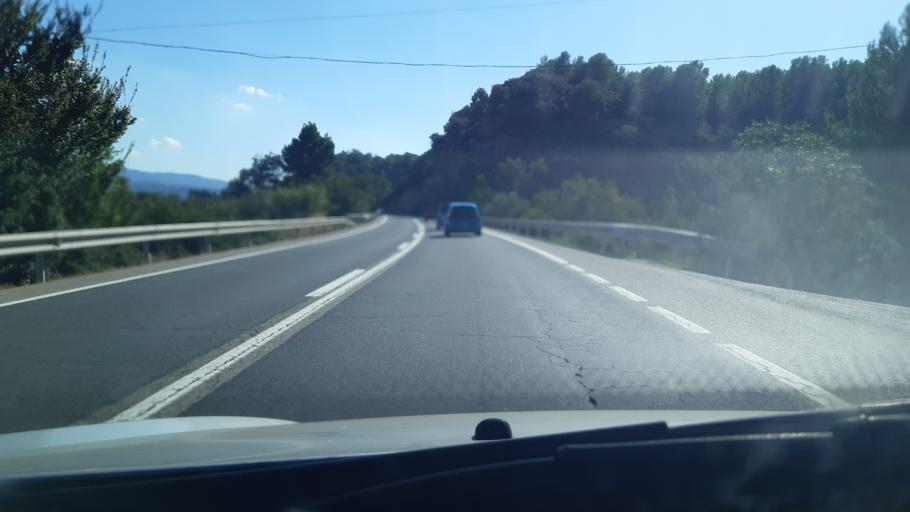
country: ES
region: Catalonia
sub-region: Provincia de Tarragona
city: Tivenys
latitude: 40.8718
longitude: 0.5013
